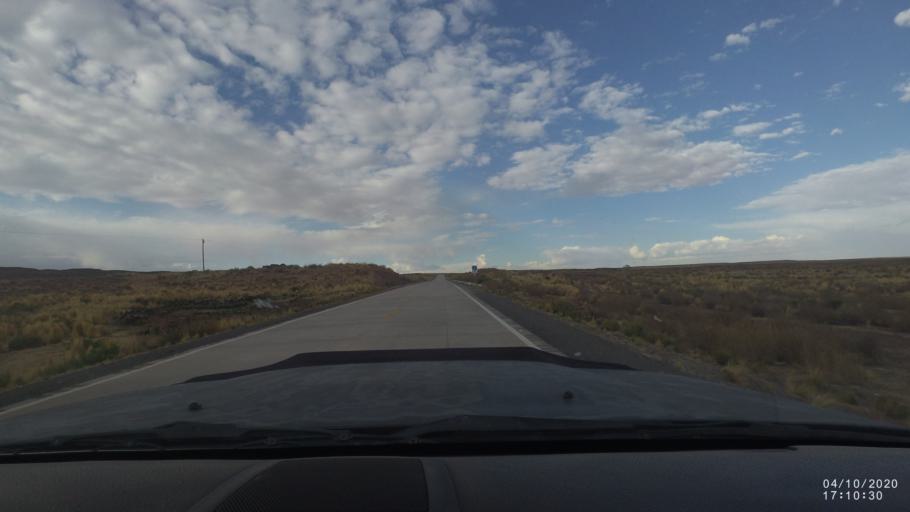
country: BO
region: Oruro
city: Oruro
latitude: -18.3305
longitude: -67.5836
